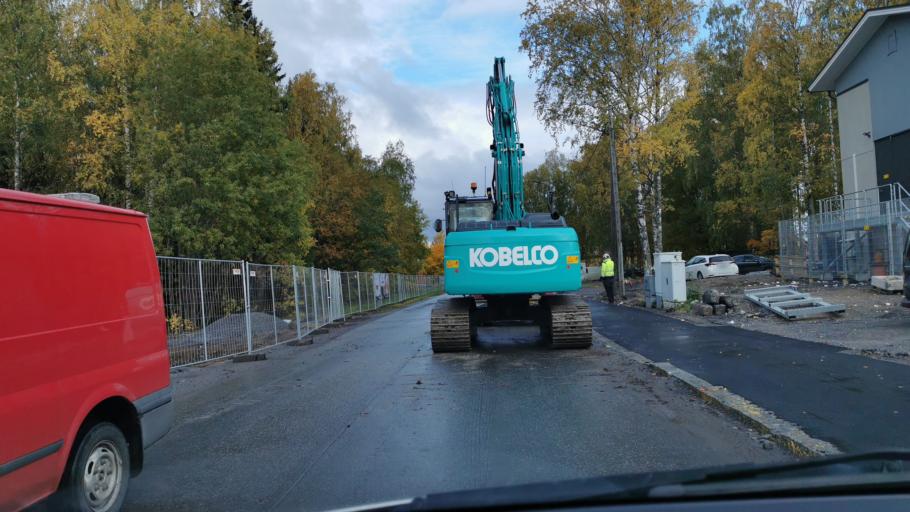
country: FI
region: Ostrobothnia
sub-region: Vaasa
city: Vaasa
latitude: 63.0914
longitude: 21.5637
